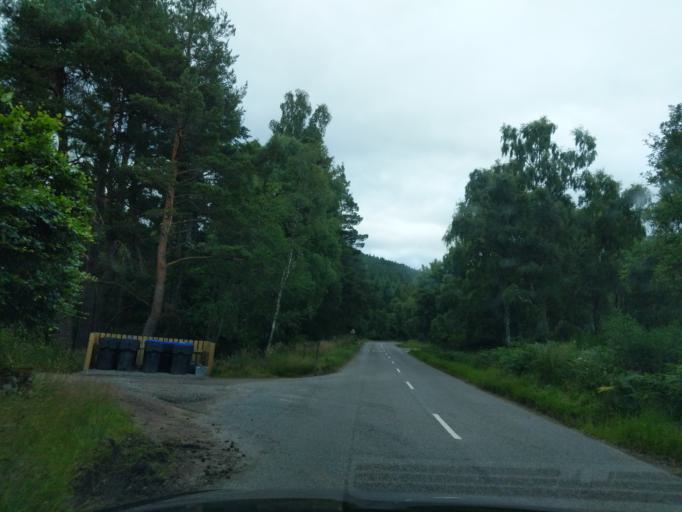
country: GB
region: Scotland
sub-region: Aberdeenshire
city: Aboyne
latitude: 57.0662
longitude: -2.8183
